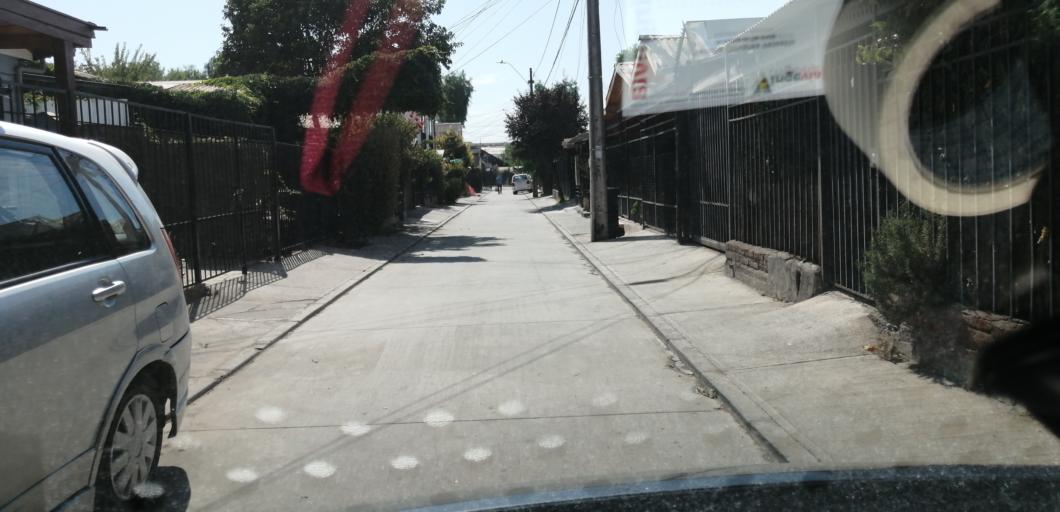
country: CL
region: Santiago Metropolitan
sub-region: Provincia de Santiago
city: Lo Prado
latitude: -33.4632
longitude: -70.7415
